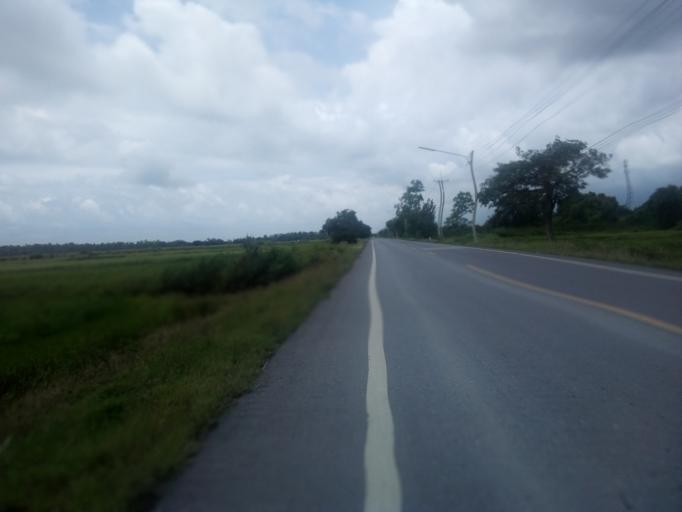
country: TH
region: Pathum Thani
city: Ban Lam Luk Ka
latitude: 14.0034
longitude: 100.8223
